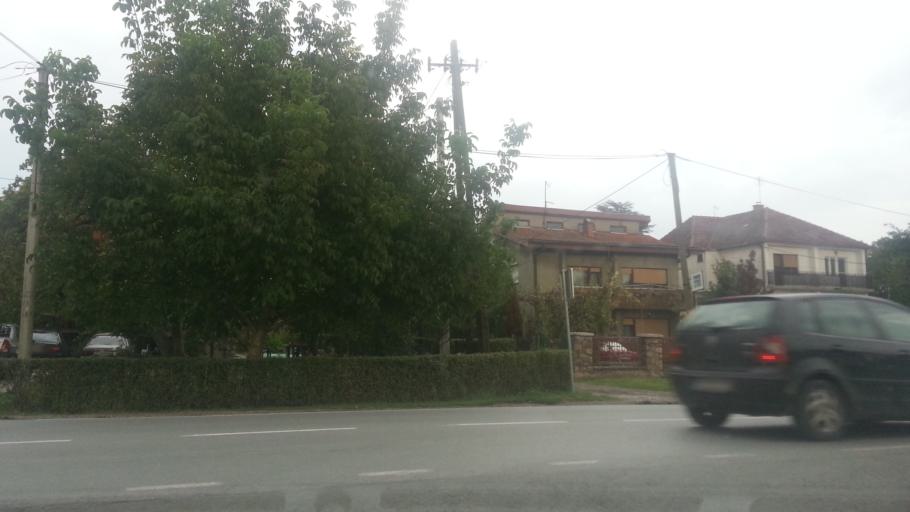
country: RS
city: Stari Banovci
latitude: 44.9725
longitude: 20.2811
